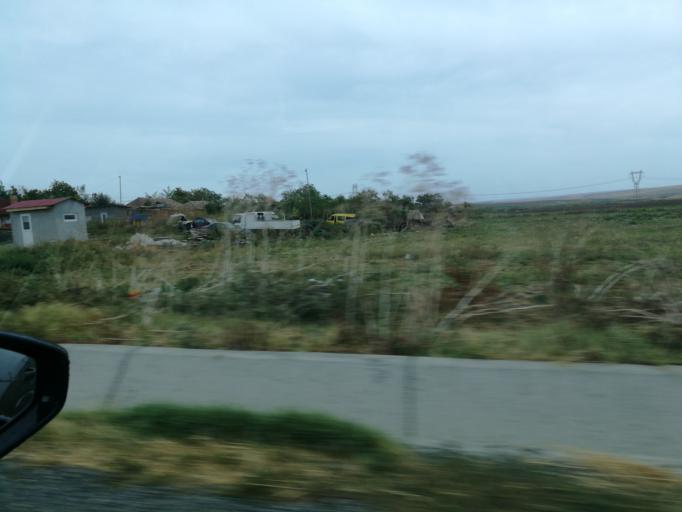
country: RO
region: Constanta
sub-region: Comuna Cogealac
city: Tariverde
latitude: 44.5539
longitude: 28.6020
